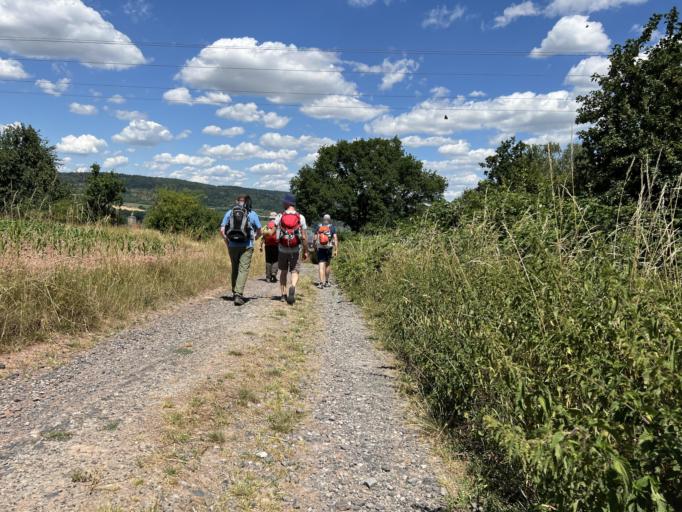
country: DE
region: Hesse
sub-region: Regierungsbezirk Darmstadt
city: Steinau an der Strasse
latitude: 50.3066
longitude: 9.4679
